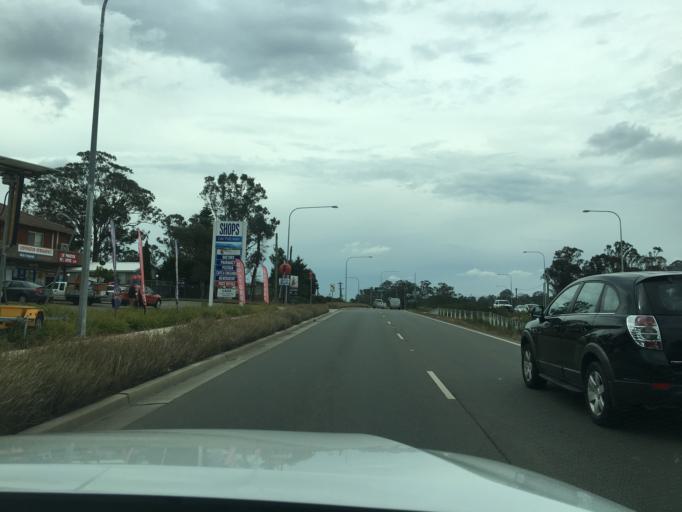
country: AU
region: New South Wales
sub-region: Campbelltown Municipality
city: Denham Court
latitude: -33.9648
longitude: 150.8169
